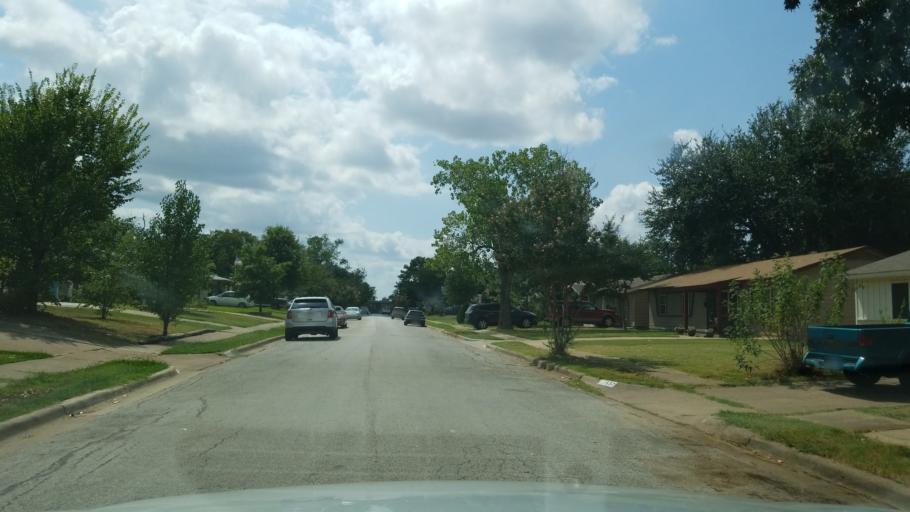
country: US
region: Texas
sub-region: Tarrant County
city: Euless
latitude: 32.8442
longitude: -97.0876
